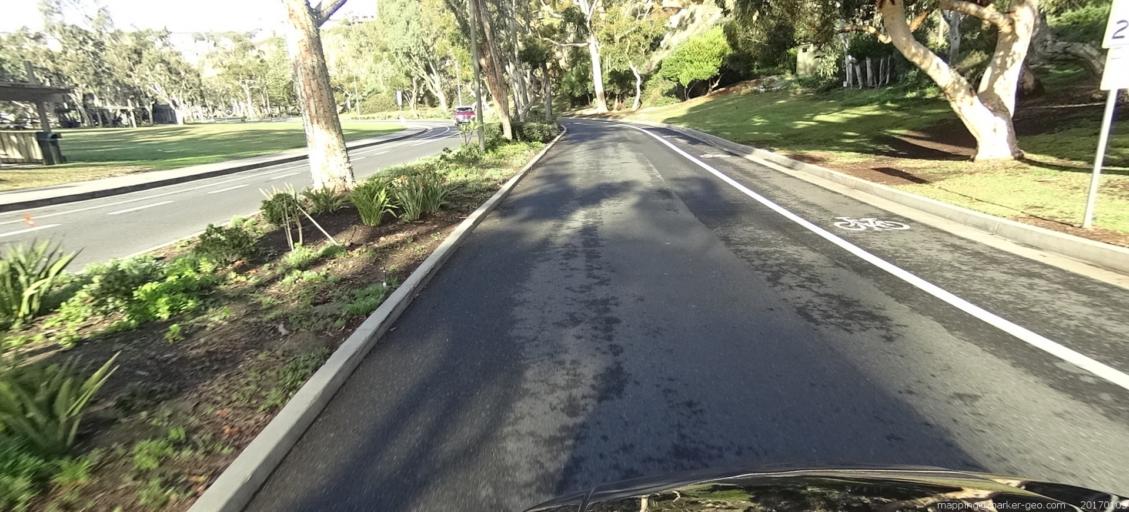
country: US
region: California
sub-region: Orange County
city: Dana Point
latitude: 33.4625
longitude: -117.6999
